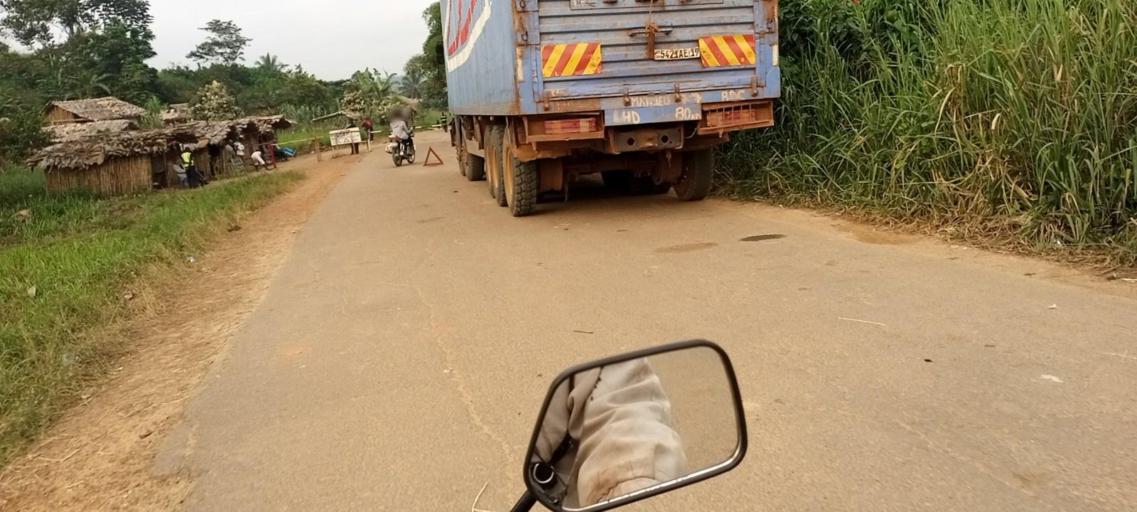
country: CD
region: Eastern Province
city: Kisangani
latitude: 0.1934
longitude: 25.5229
